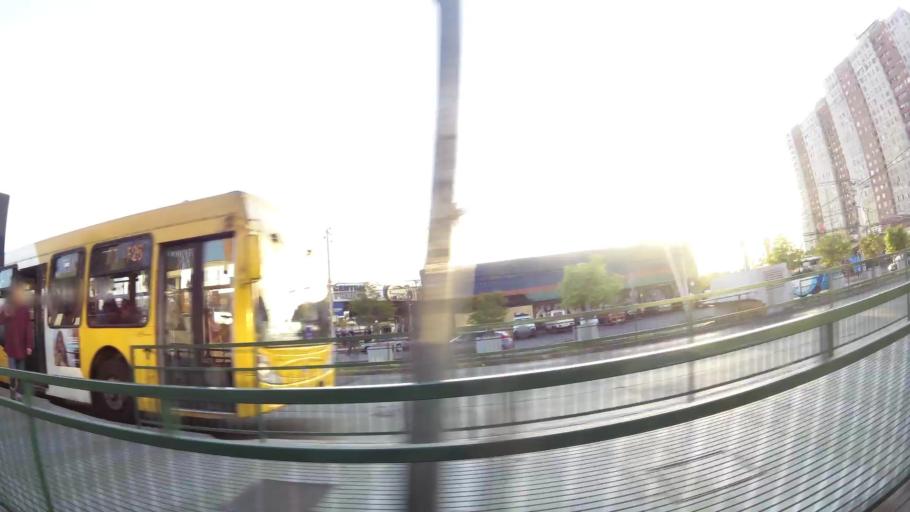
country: CL
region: Santiago Metropolitan
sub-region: Provincia de Santiago
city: La Pintana
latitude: -33.5270
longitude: -70.5965
